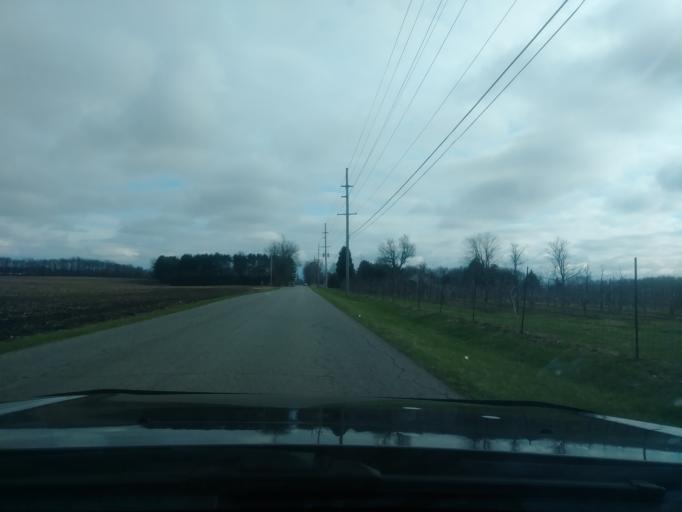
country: US
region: Indiana
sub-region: LaPorte County
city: LaPorte
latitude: 41.6032
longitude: -86.7978
